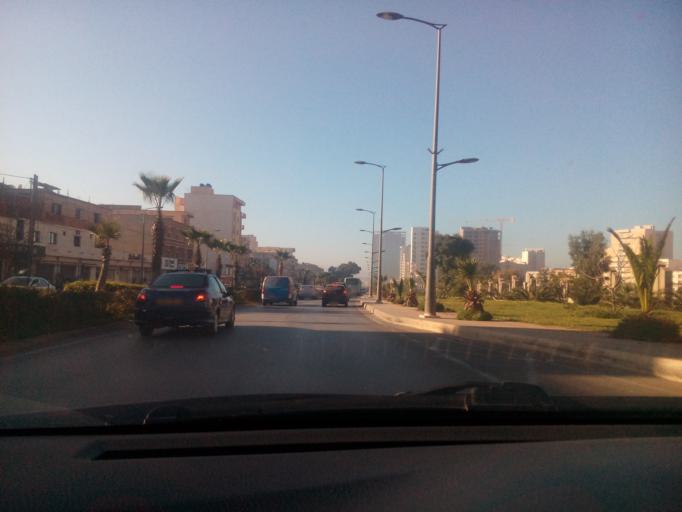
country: DZ
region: Oran
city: Bir el Djir
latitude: 35.7341
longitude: -0.5790
